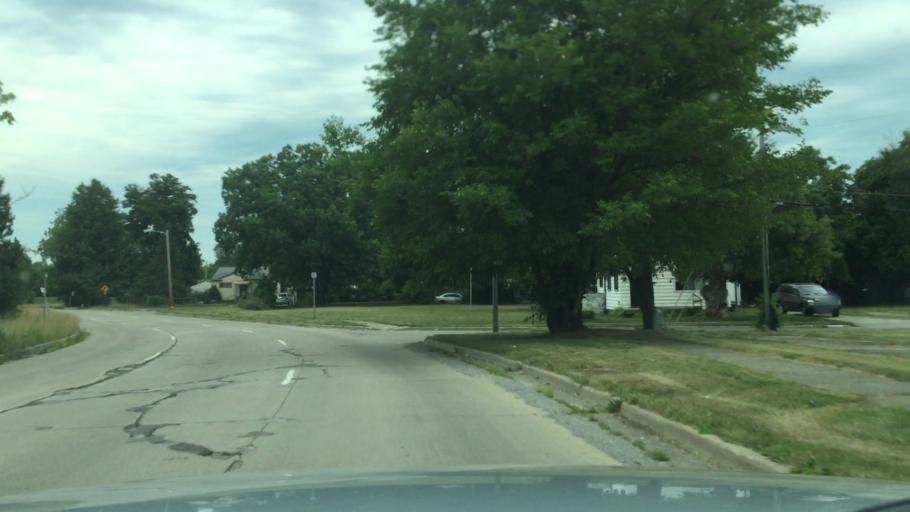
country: US
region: Michigan
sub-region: Genesee County
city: Beecher
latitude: 43.0659
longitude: -83.6812
